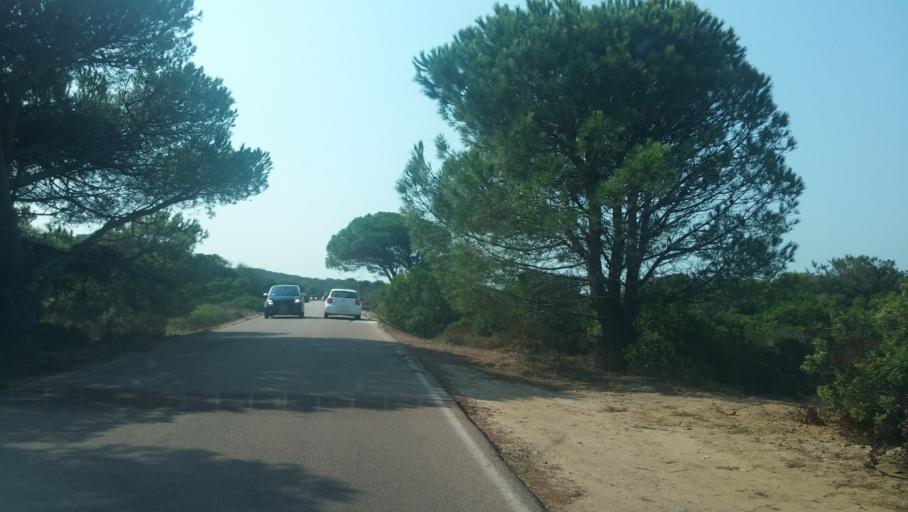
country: IT
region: Sardinia
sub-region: Provincia di Olbia-Tempio
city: La Maddalena
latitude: 41.1986
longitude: 9.4574
